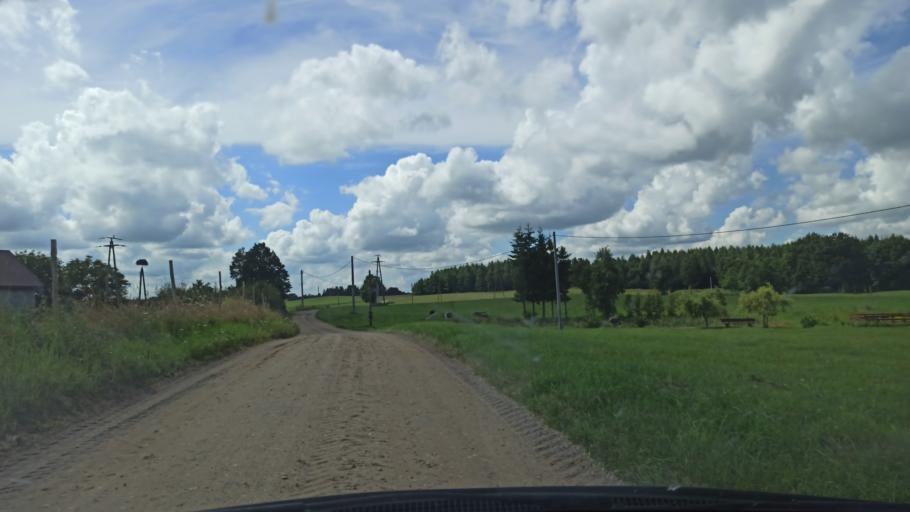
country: PL
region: Warmian-Masurian Voivodeship
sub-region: Powiat ostrodzki
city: Morag
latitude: 53.8644
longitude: 20.0387
